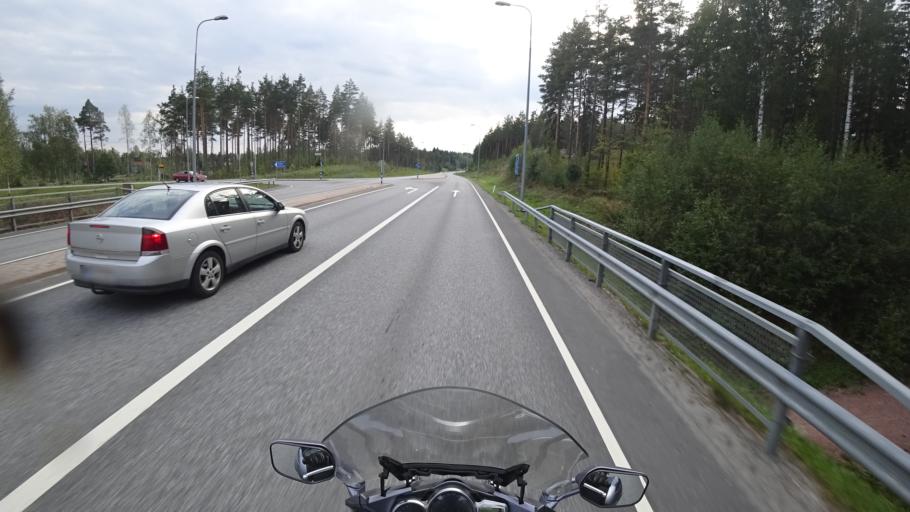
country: FI
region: Uusimaa
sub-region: Raaseporin
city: Karis
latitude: 60.0740
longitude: 23.6519
